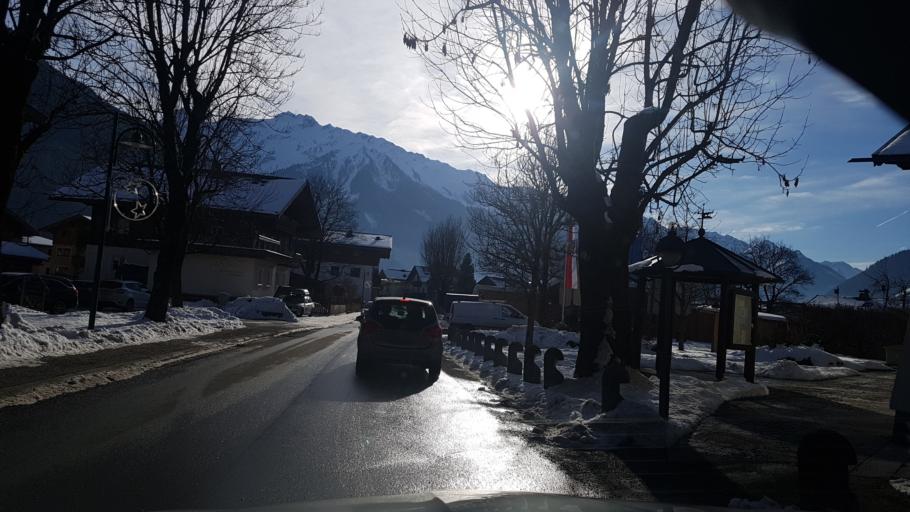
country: AT
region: Salzburg
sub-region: Politischer Bezirk Zell am See
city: Bramberg am Wildkogel
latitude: 47.2723
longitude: 12.3461
